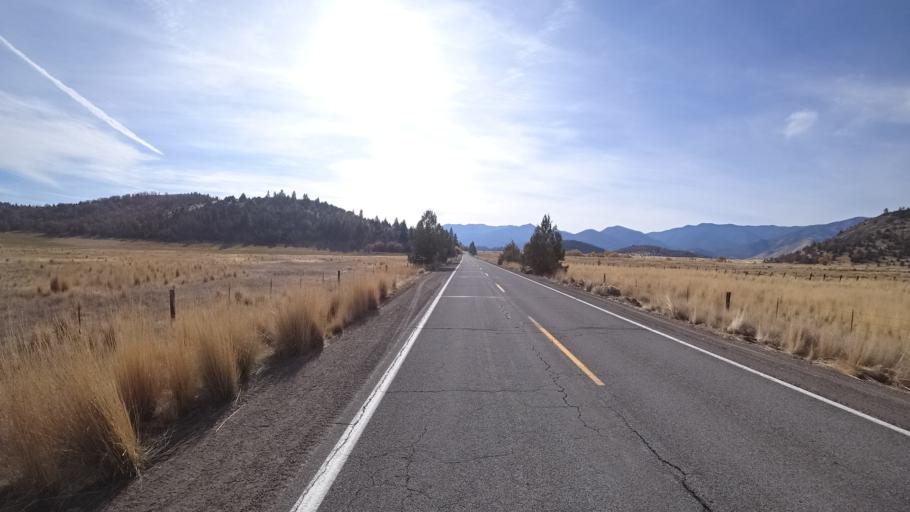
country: US
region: California
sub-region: Siskiyou County
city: Weed
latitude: 41.4844
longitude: -122.4094
